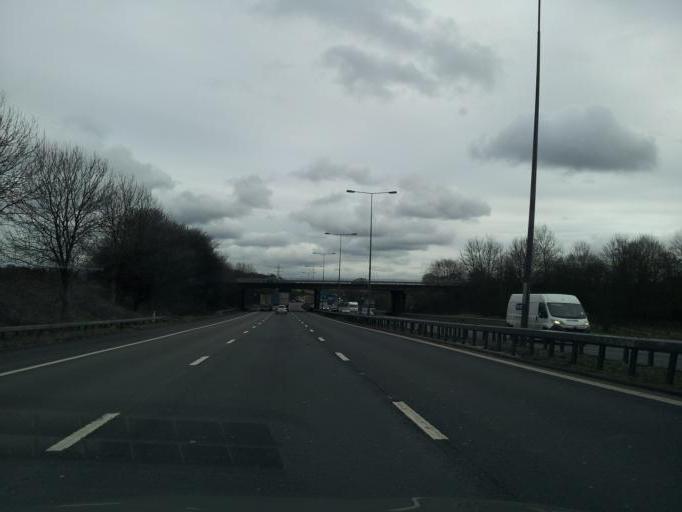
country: GB
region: England
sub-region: Staffordshire
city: Newcastle under Lyme
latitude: 52.9887
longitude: -2.2588
